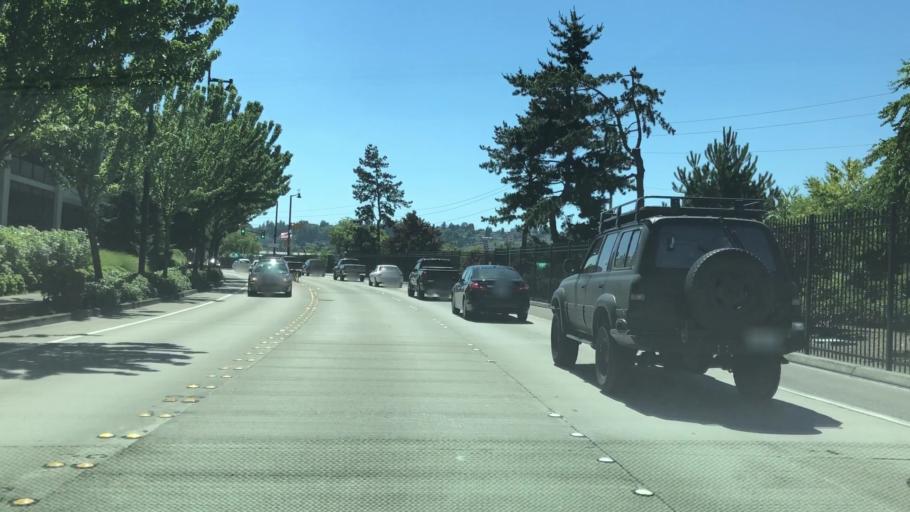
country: US
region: Washington
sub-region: King County
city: Renton
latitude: 47.4989
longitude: -122.2050
